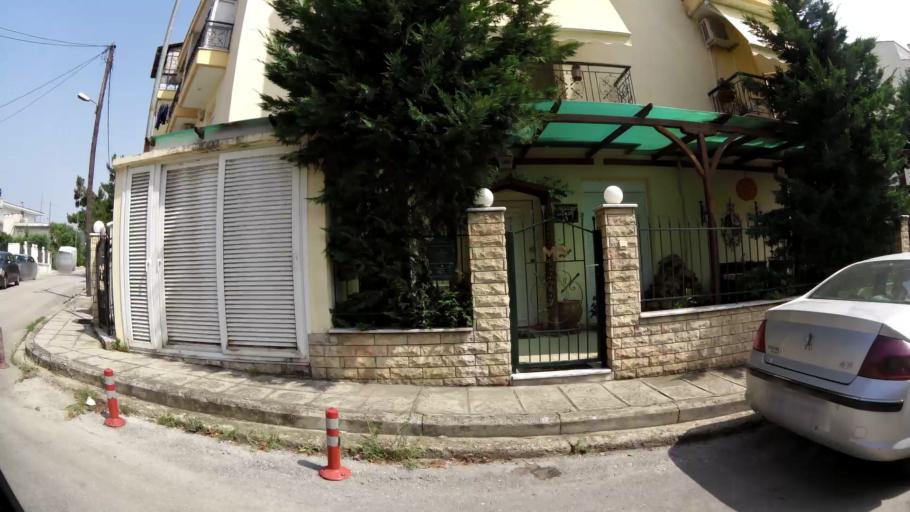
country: GR
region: Central Macedonia
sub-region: Nomos Thessalonikis
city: Efkarpia
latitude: 40.6919
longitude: 22.9549
